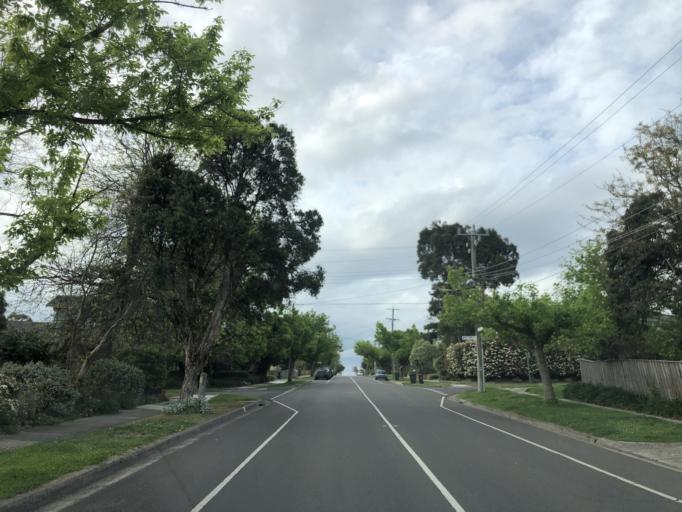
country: AU
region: Victoria
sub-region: Monash
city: Ashwood
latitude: -37.8668
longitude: 145.1189
